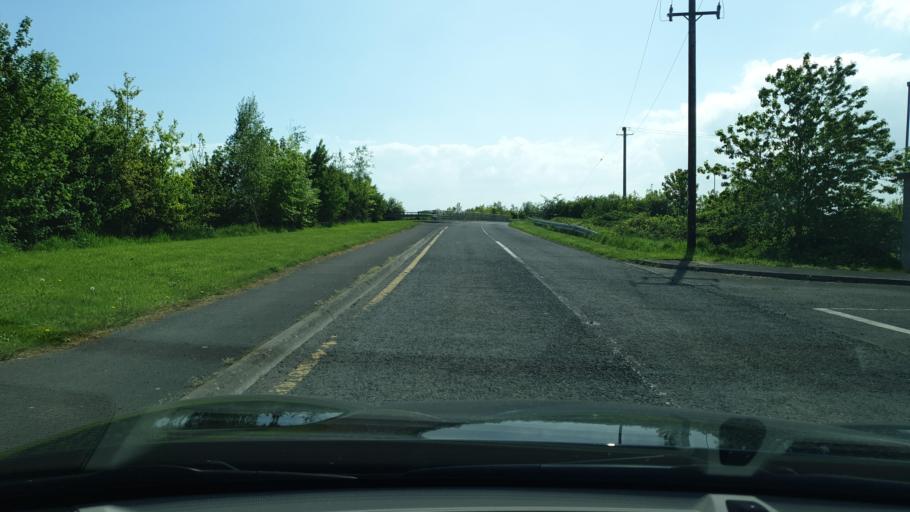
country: IE
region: Leinster
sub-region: An Mhi
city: Dunshaughlin
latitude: 53.4917
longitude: -6.5297
